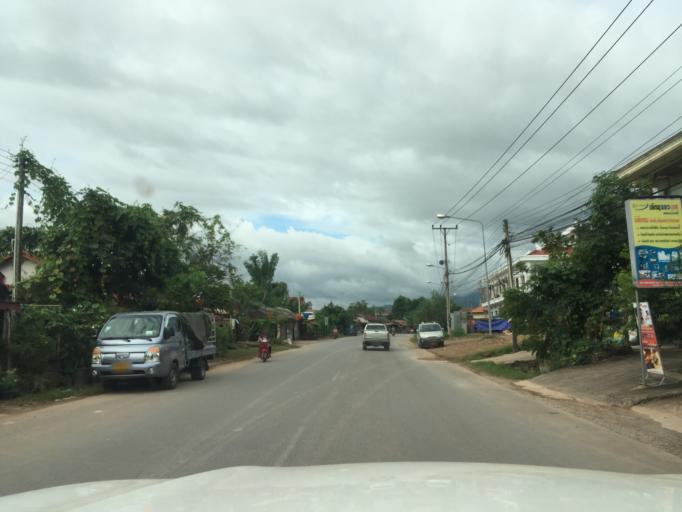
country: LA
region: Oudomxai
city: Muang Xay
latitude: 20.6990
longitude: 101.9913
